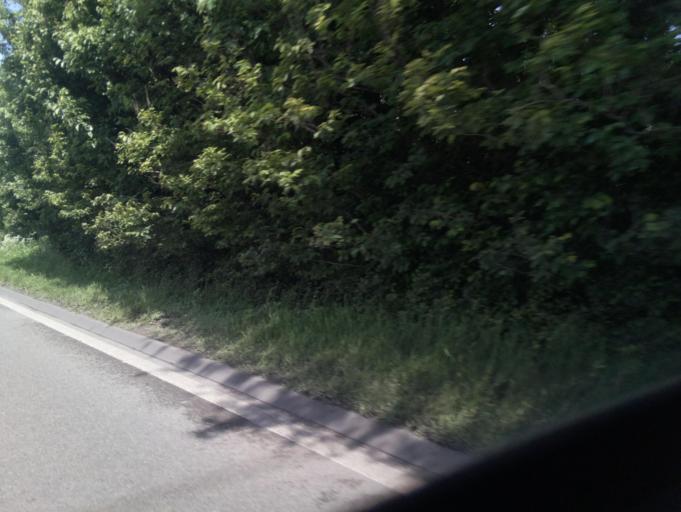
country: GB
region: England
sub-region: North Lincolnshire
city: Broughton
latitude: 53.5549
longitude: -0.5832
